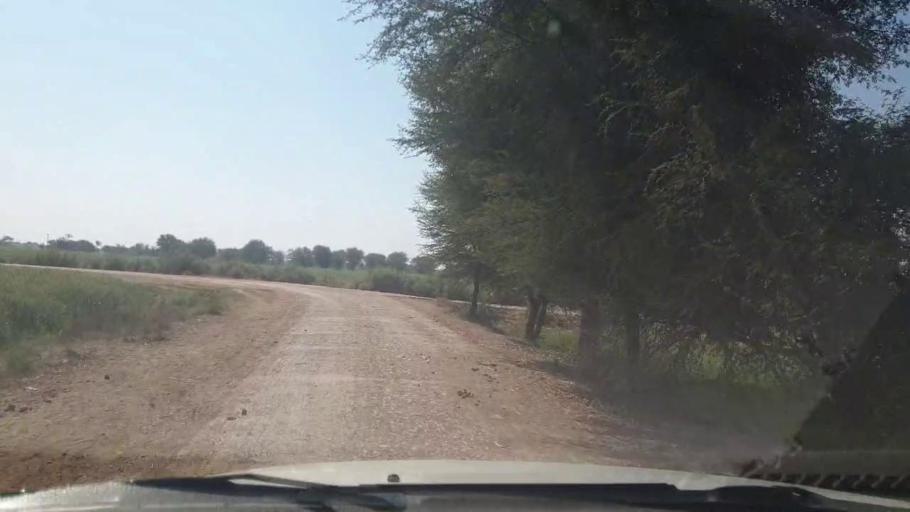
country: PK
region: Sindh
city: Mirpur Khas
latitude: 25.6025
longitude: 69.1880
